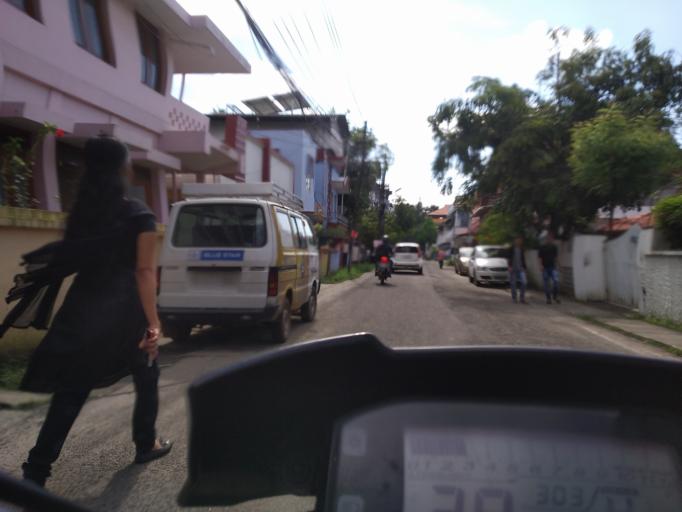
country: IN
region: Kerala
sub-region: Ernakulam
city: Cochin
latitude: 9.9849
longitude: 76.2859
